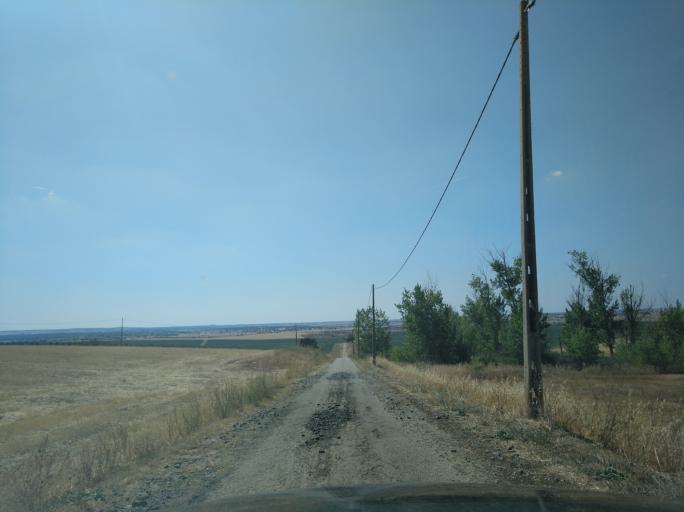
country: PT
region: Portalegre
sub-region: Campo Maior
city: Campo Maior
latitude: 39.0233
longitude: -7.1178
